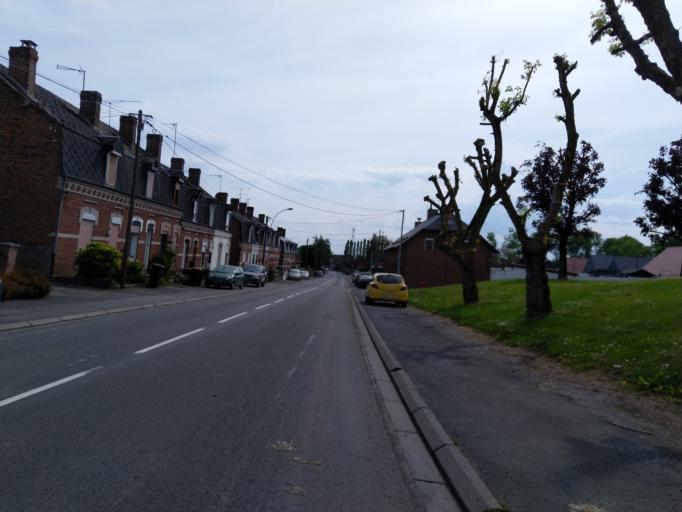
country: FR
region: Picardie
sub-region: Departement de l'Aisne
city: Boue
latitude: 50.0046
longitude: 3.6847
